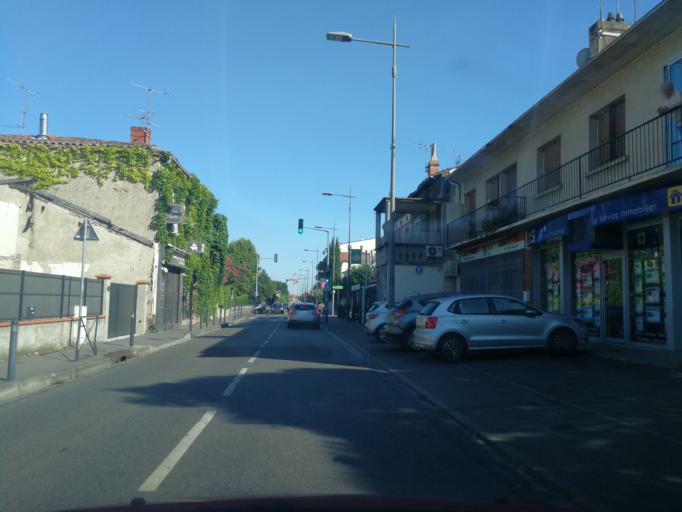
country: FR
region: Midi-Pyrenees
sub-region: Departement de la Haute-Garonne
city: Balma
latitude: 43.6169
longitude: 1.4724
